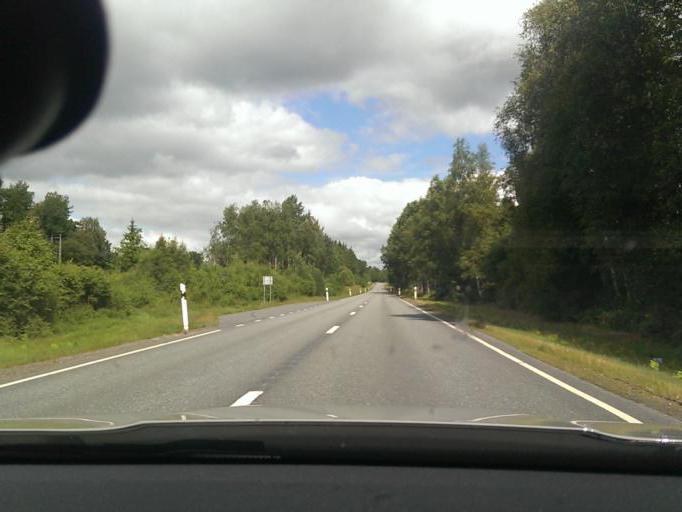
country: SE
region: Joenkoeping
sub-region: Varnamo Kommun
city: Varnamo
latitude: 57.2196
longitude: 14.0137
